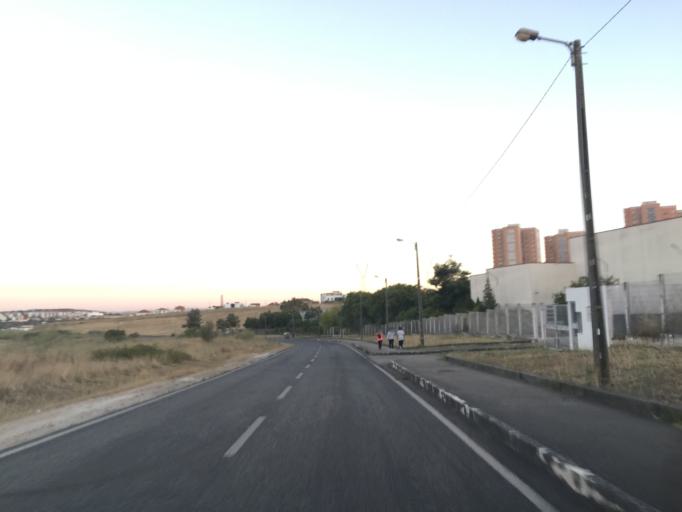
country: PT
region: Lisbon
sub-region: Odivelas
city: Povoa de Santo Adriao
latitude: 38.8131
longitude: -9.1750
